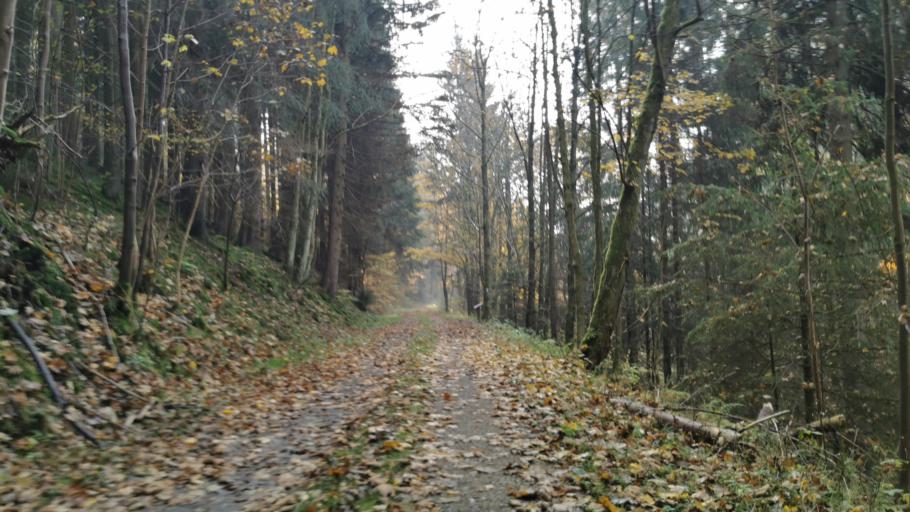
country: DE
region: Bavaria
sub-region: Upper Franconia
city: Nordhalben
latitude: 50.3880
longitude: 11.5304
